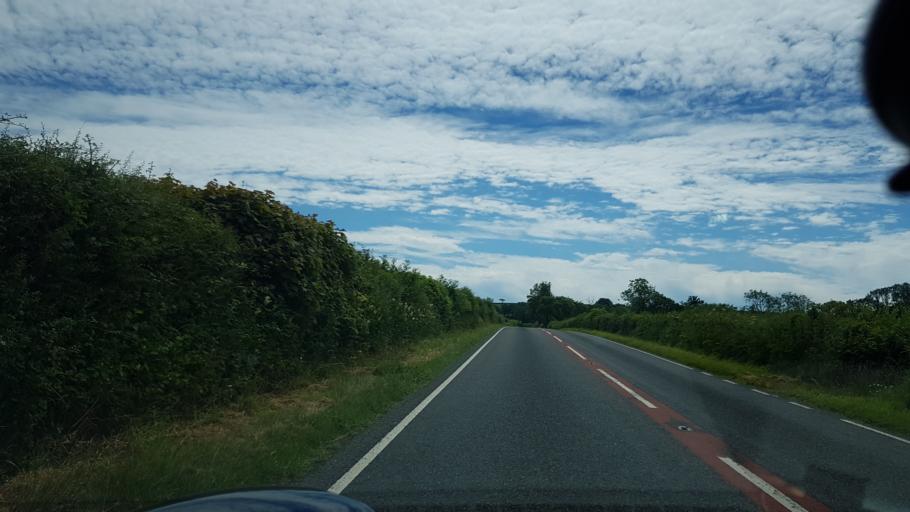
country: GB
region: Wales
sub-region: Carmarthenshire
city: Saint Clears
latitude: 51.7937
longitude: -4.4851
